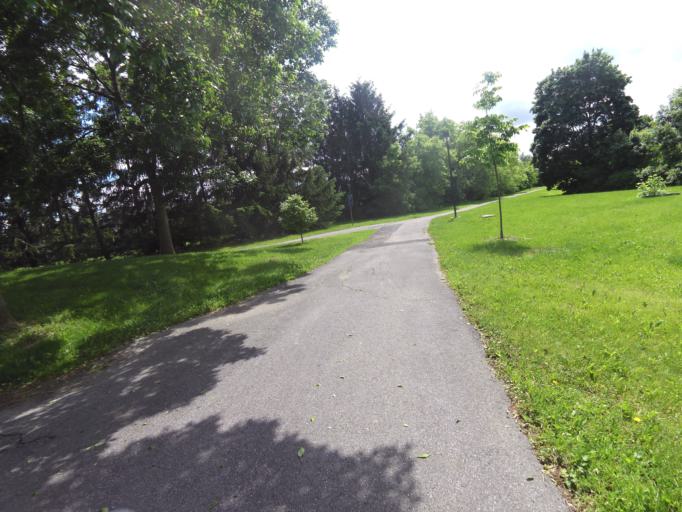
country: CA
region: Ontario
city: Ottawa
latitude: 45.3627
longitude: -75.6406
